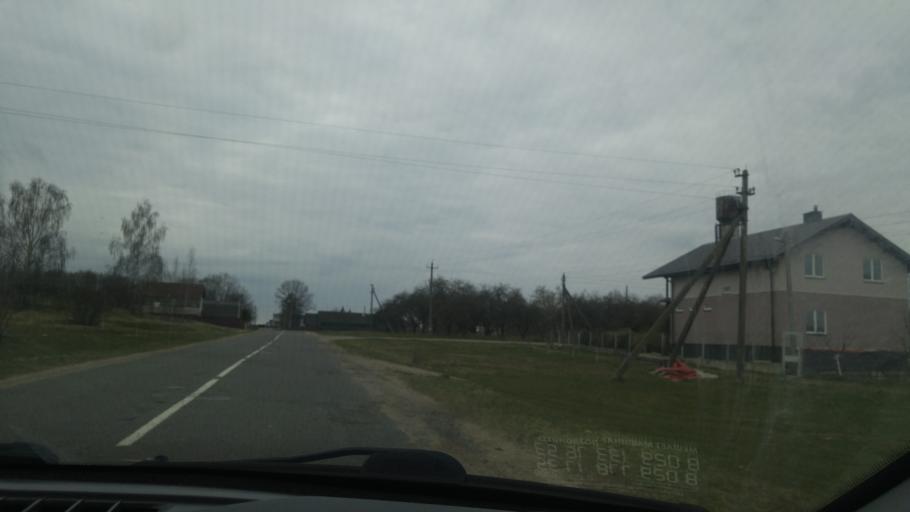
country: BY
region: Minsk
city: Blon'
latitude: 53.6765
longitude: 28.1831
